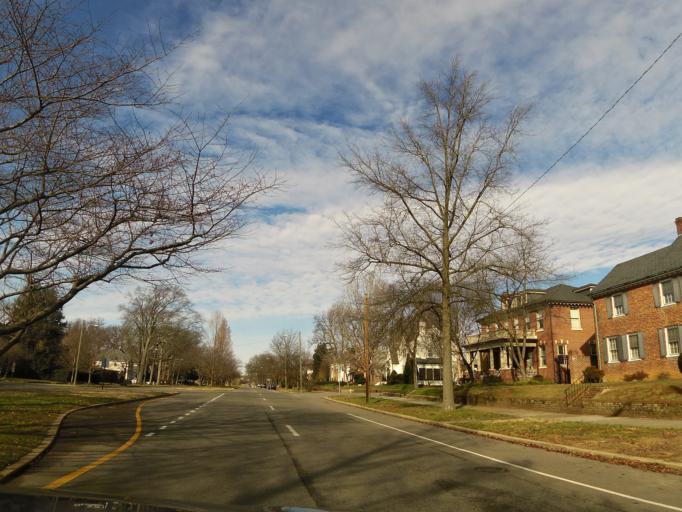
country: US
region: Virginia
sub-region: Henrico County
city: Dumbarton
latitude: 37.5724
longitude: -77.4911
